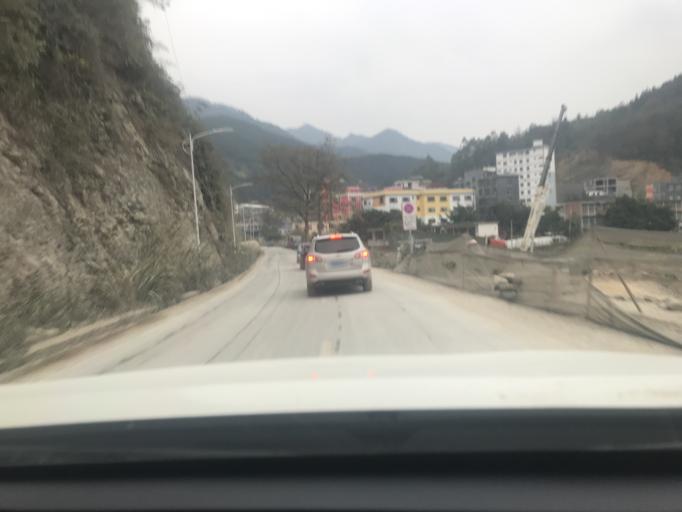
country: CN
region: Guangxi Zhuangzu Zizhiqu
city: Xinzhou
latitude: 24.9848
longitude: 105.8186
